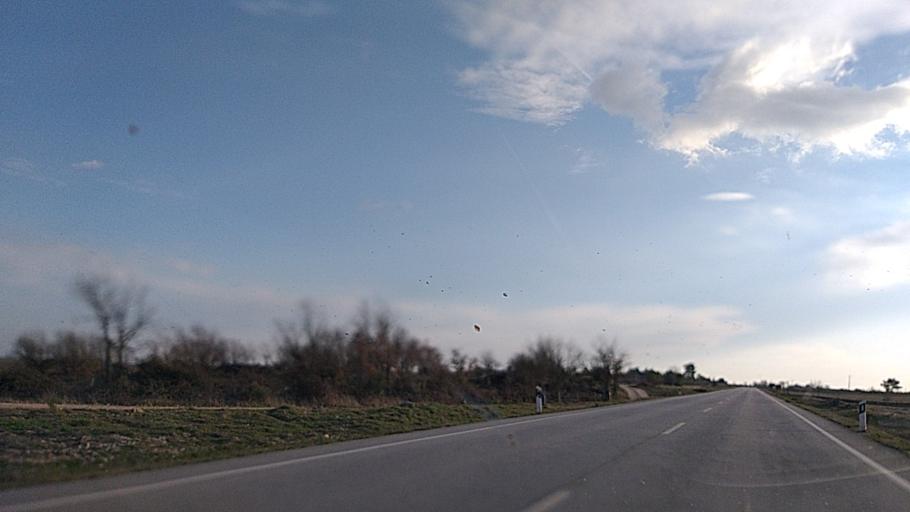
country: ES
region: Castille and Leon
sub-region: Provincia de Salamanca
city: Fuentes de Onoro
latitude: 40.6216
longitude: -6.9778
